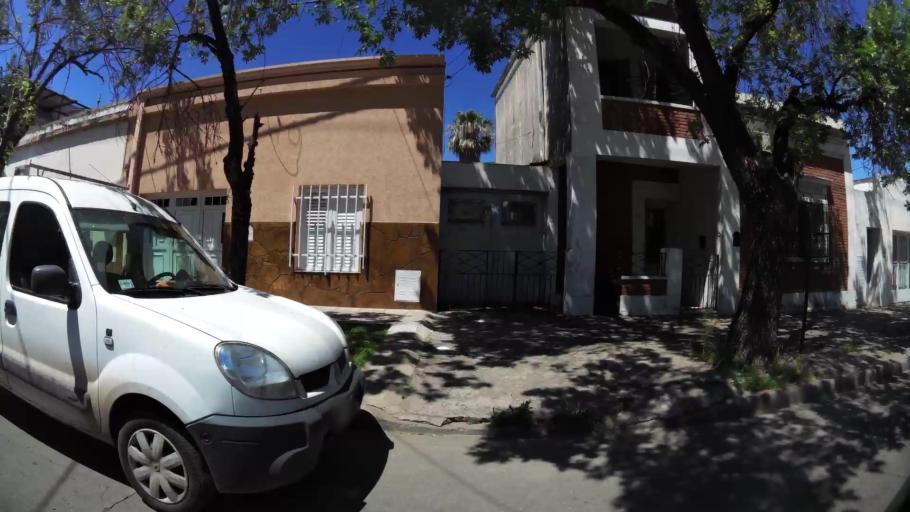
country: AR
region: Santa Fe
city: Santa Fe de la Vera Cruz
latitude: -31.6294
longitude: -60.7144
